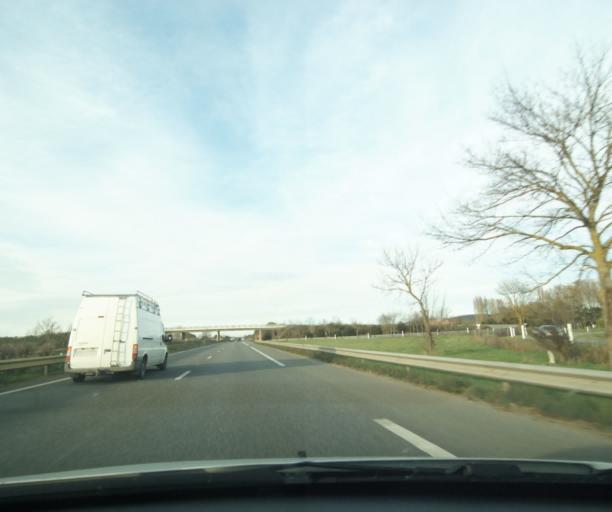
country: FR
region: Midi-Pyrenees
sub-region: Departement de la Haute-Garonne
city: Le Fauga
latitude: 43.3972
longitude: 1.2886
